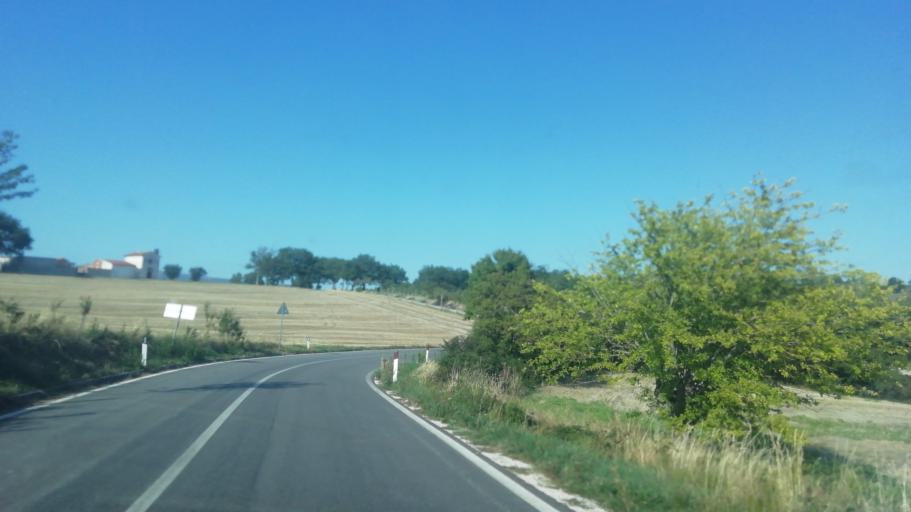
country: IT
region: The Marches
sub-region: Provincia di Pesaro e Urbino
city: Frontone
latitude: 43.5378
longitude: 12.7381
